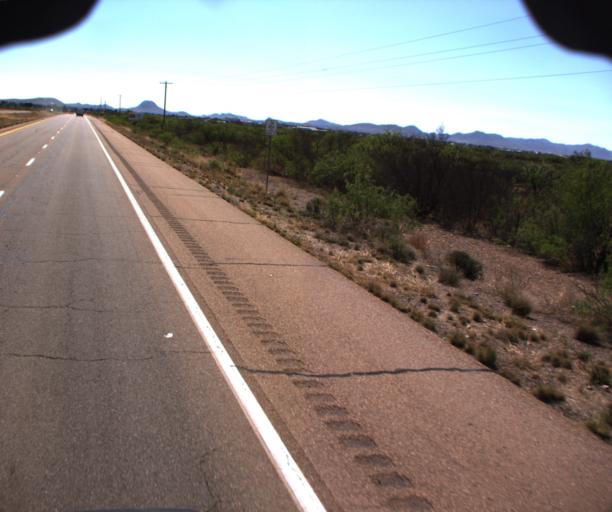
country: US
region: Arizona
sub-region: Cochise County
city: Pirtleville
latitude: 31.3519
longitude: -109.5764
